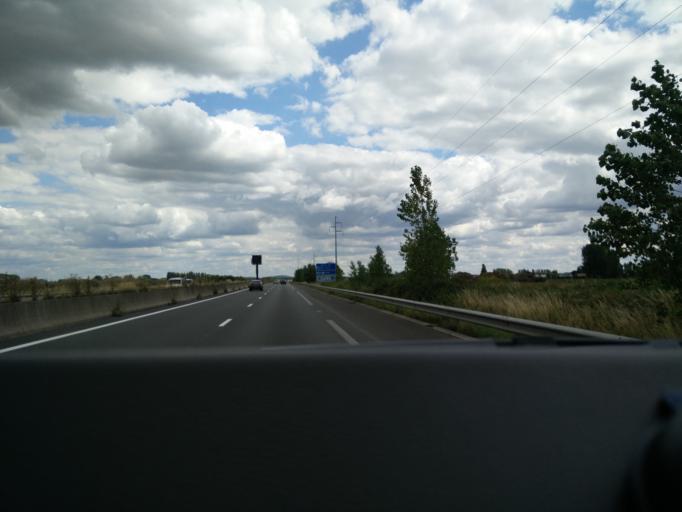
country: FR
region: Nord-Pas-de-Calais
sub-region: Departement du Nord
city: Wormhout
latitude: 50.9023
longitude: 2.4947
